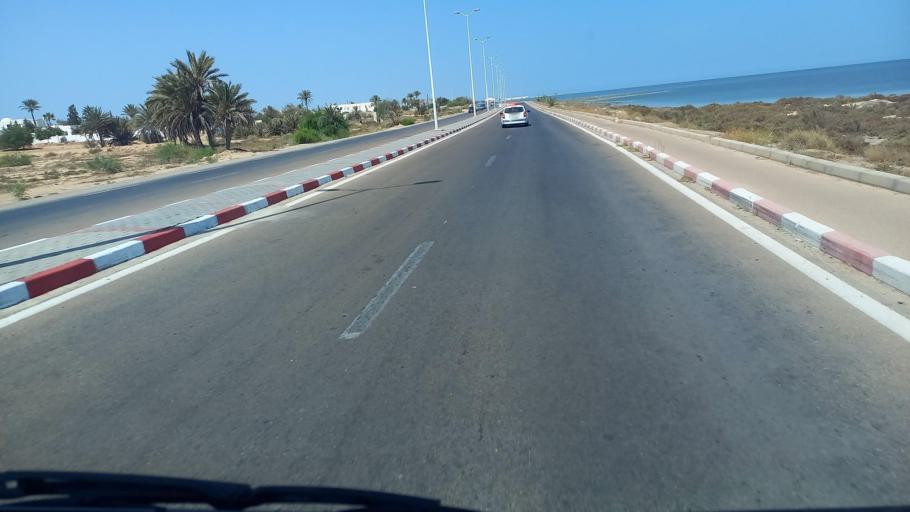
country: TN
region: Madanin
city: Houmt Souk
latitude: 33.8737
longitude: 10.9076
